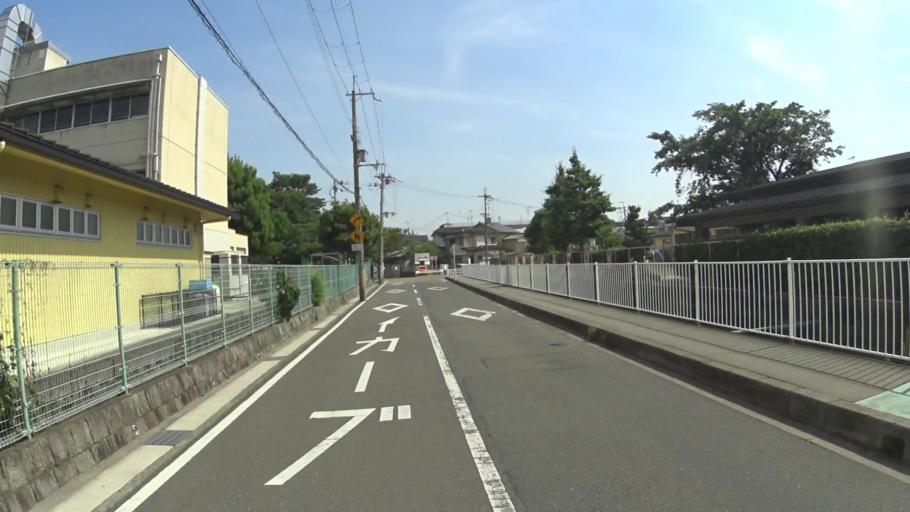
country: JP
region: Kyoto
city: Muko
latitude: 34.9597
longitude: 135.7007
